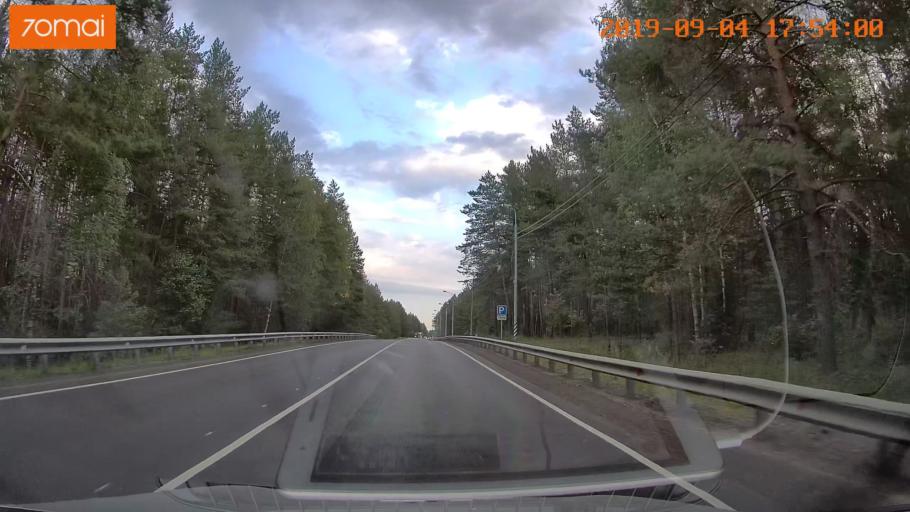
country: RU
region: Moskovskaya
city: Imeni Tsyurupy
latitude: 55.5130
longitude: 38.7340
